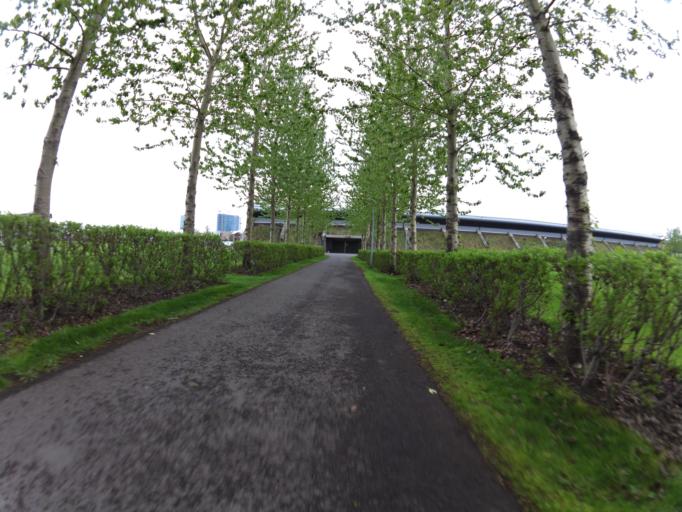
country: IS
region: Capital Region
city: Kopavogur
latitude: 64.1036
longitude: -21.9013
